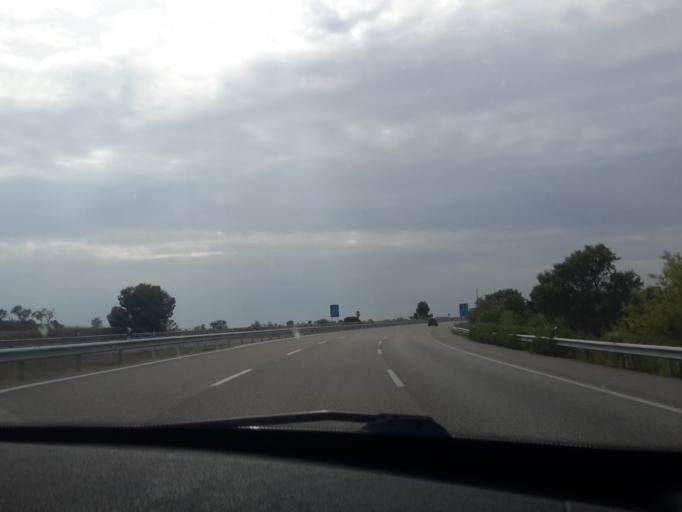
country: ES
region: Aragon
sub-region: Provincia de Huesca
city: Fraga
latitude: 41.4643
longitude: 0.2775
